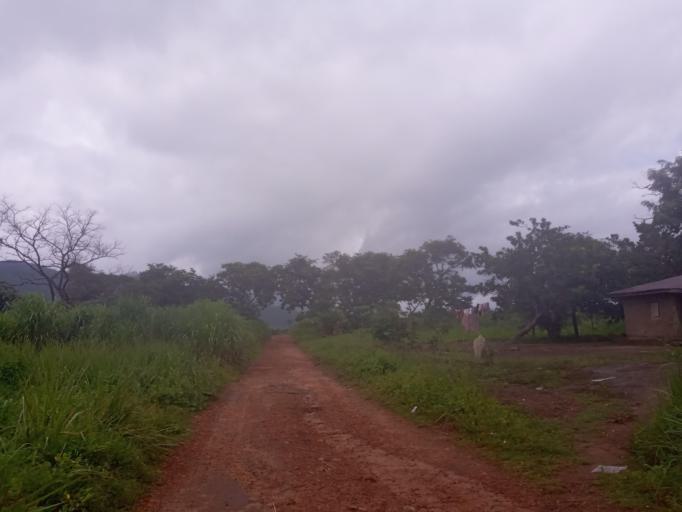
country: SL
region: Northern Province
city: Bumbuna
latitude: 8.9511
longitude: -11.7578
